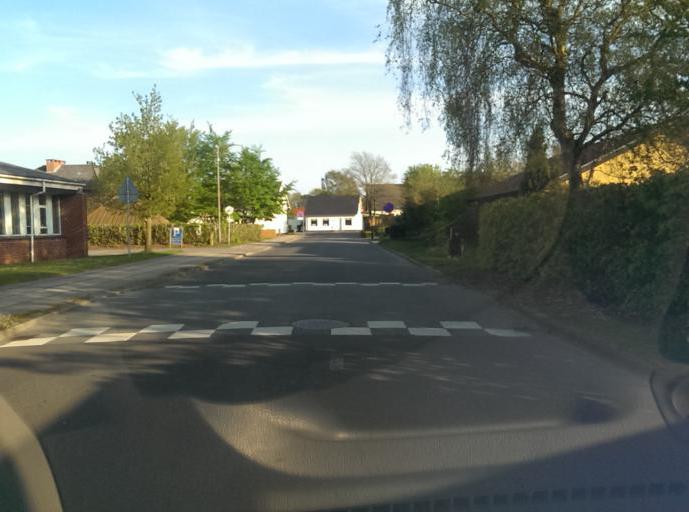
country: DK
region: South Denmark
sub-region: Esbjerg Kommune
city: Bramming
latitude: 55.4684
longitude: 8.7014
